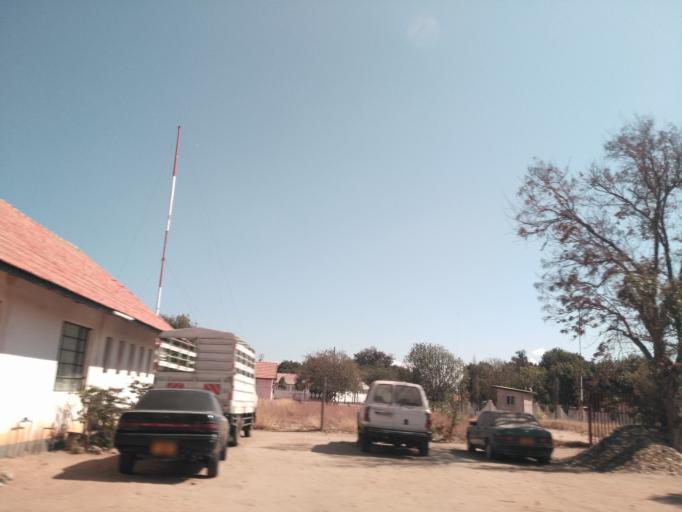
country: TZ
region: Dodoma
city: Dodoma
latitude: -6.1695
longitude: 35.7463
